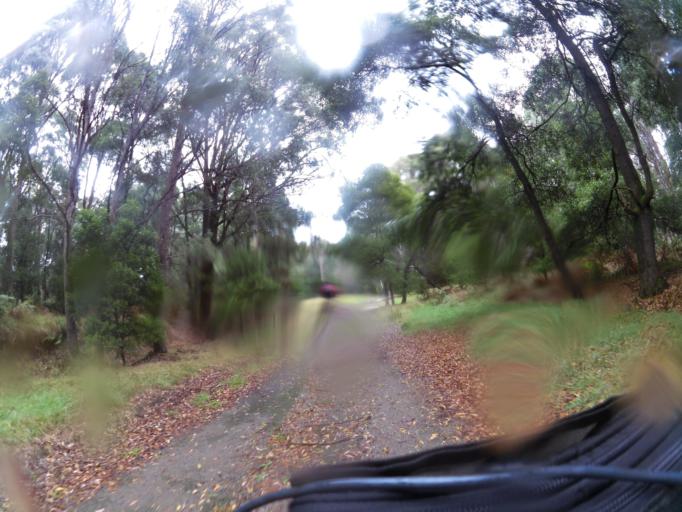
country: AU
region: New South Wales
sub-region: Greater Hume Shire
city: Holbrook
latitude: -36.1896
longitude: 147.5434
